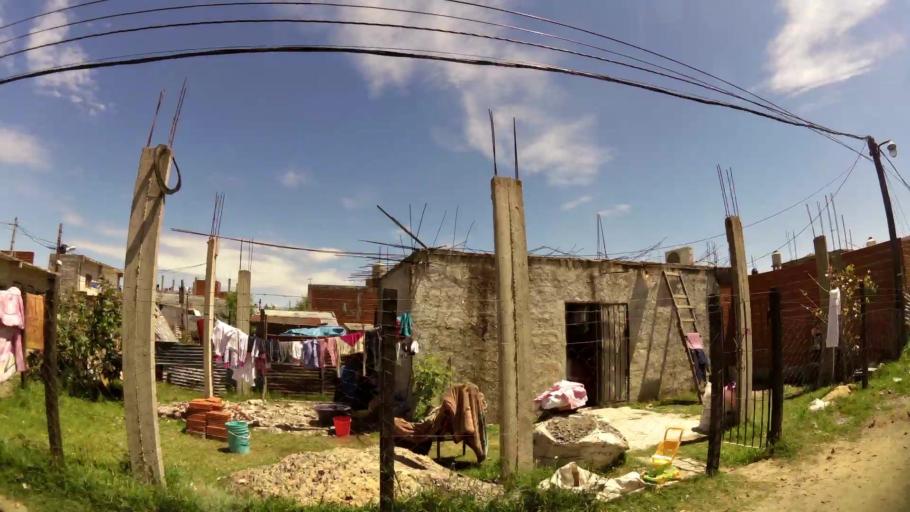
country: AR
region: Buenos Aires
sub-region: Partido de Quilmes
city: Quilmes
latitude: -34.7283
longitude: -58.3164
